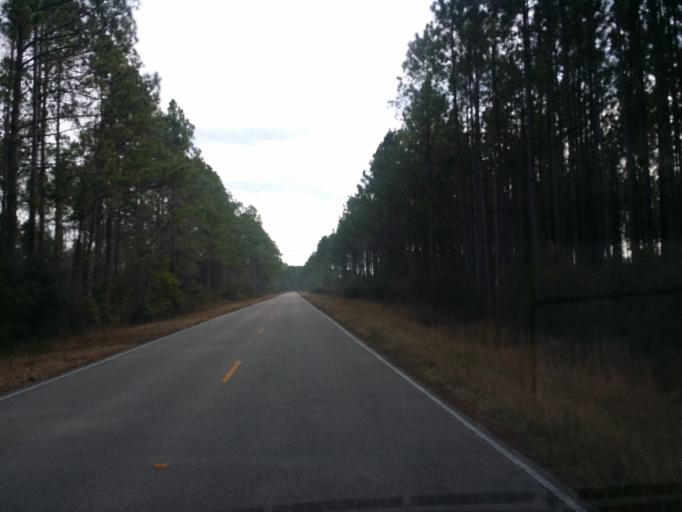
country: US
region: Florida
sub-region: Leon County
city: Woodville
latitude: 30.1808
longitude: -84.1644
